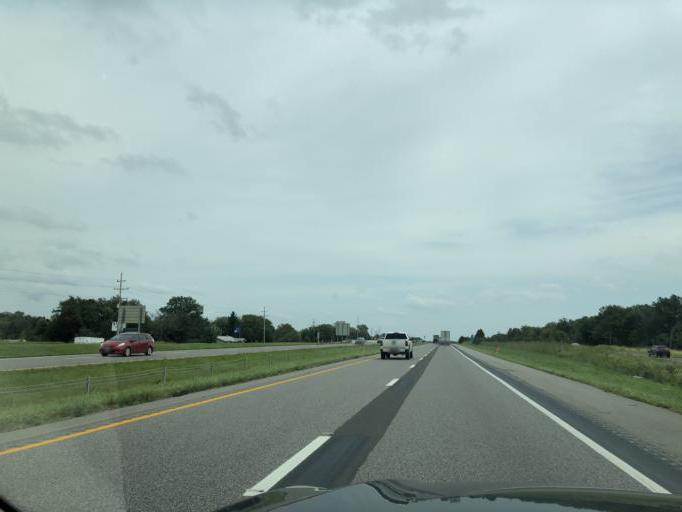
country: US
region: Missouri
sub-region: Saint Charles County
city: Wentzville
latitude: 38.8089
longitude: -90.9246
